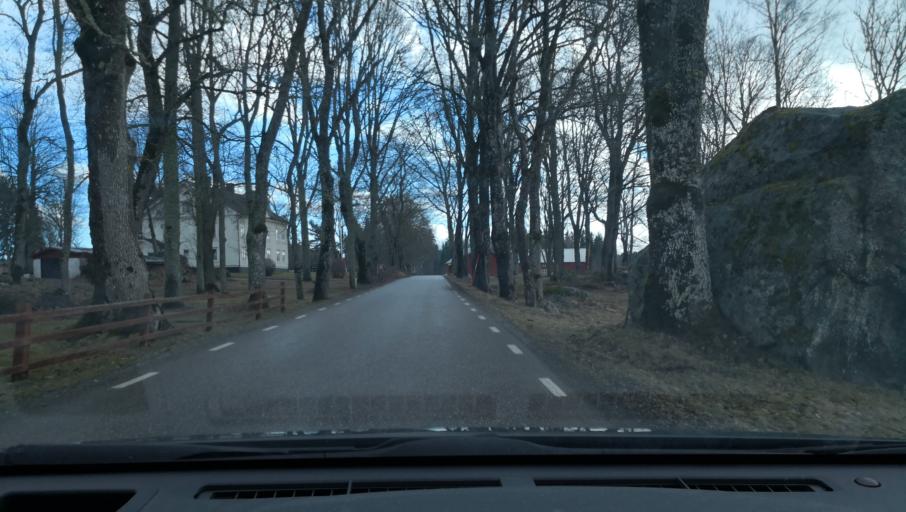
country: SE
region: OErebro
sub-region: Lindesbergs Kommun
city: Fellingsbro
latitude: 59.3470
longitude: 15.6862
